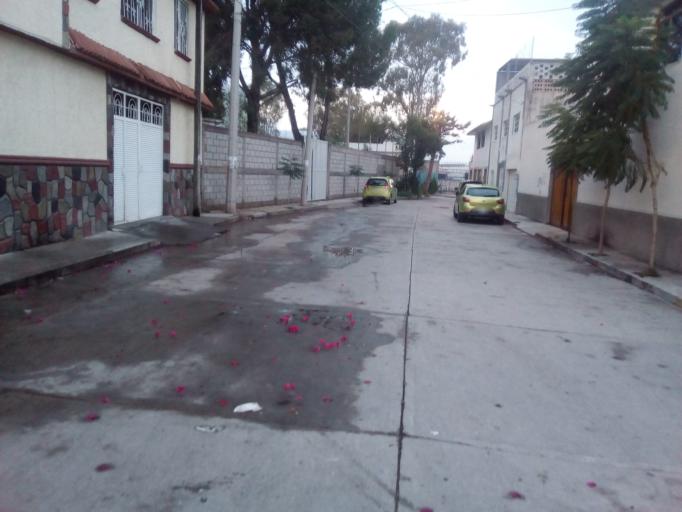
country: MX
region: Guerrero
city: San Luis de la Paz
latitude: 21.2925
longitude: -100.5247
